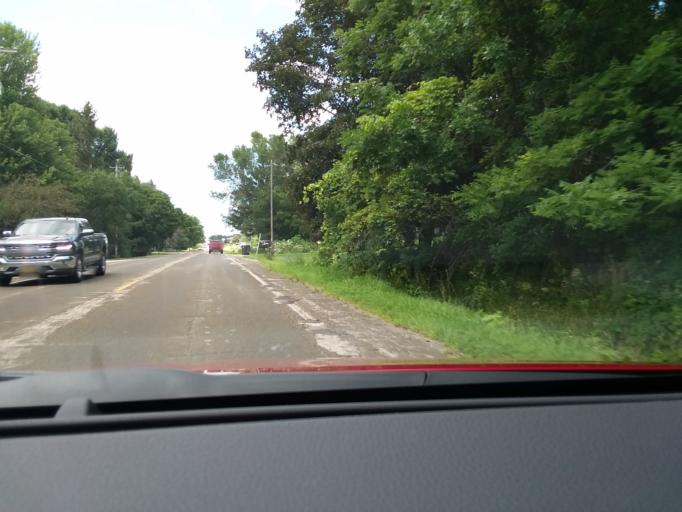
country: US
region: Wisconsin
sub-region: Dane County
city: De Forest
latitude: 43.2333
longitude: -89.3436
